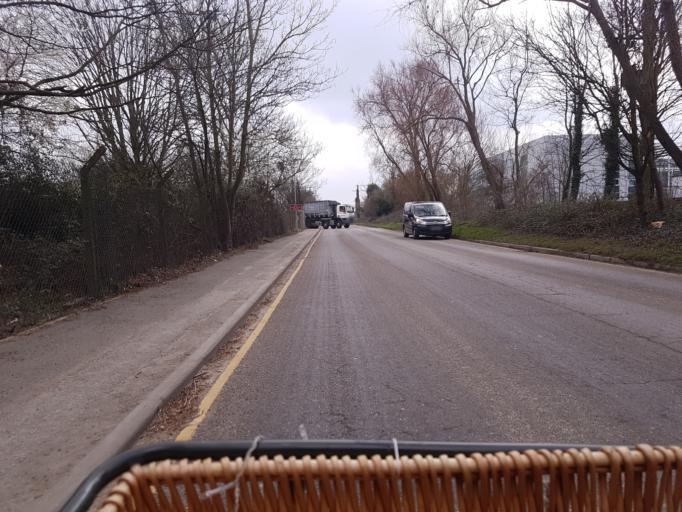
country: GB
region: England
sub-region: Cambridgeshire
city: Cambridge
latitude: 52.2292
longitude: 0.1544
